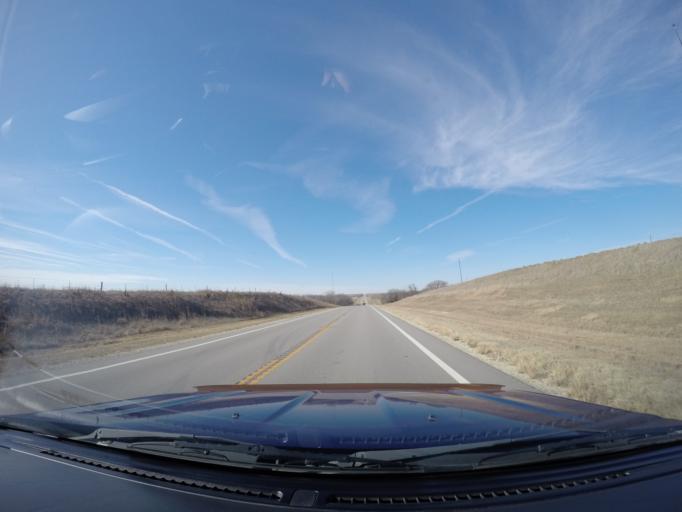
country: US
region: Kansas
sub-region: Cloud County
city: Concordia
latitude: 39.3647
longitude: -97.6441
